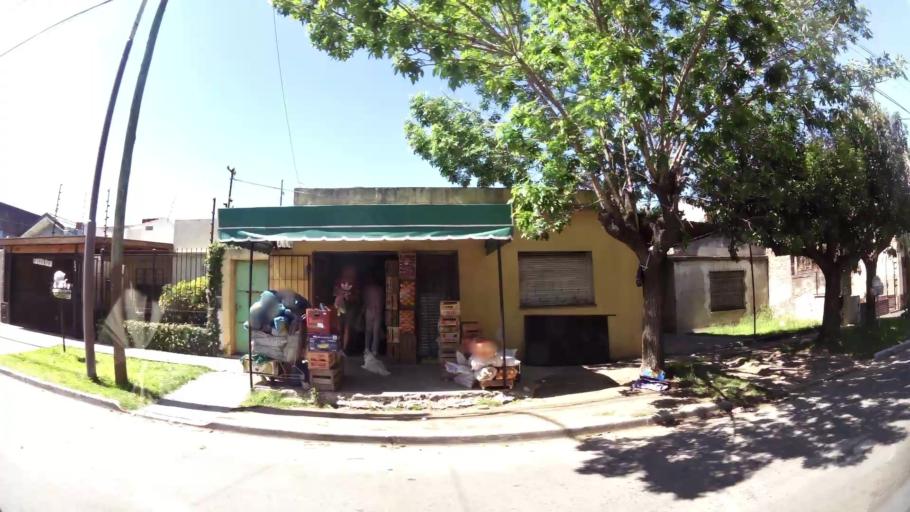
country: AR
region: Buenos Aires
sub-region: Partido de Quilmes
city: Quilmes
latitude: -34.7272
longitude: -58.2962
